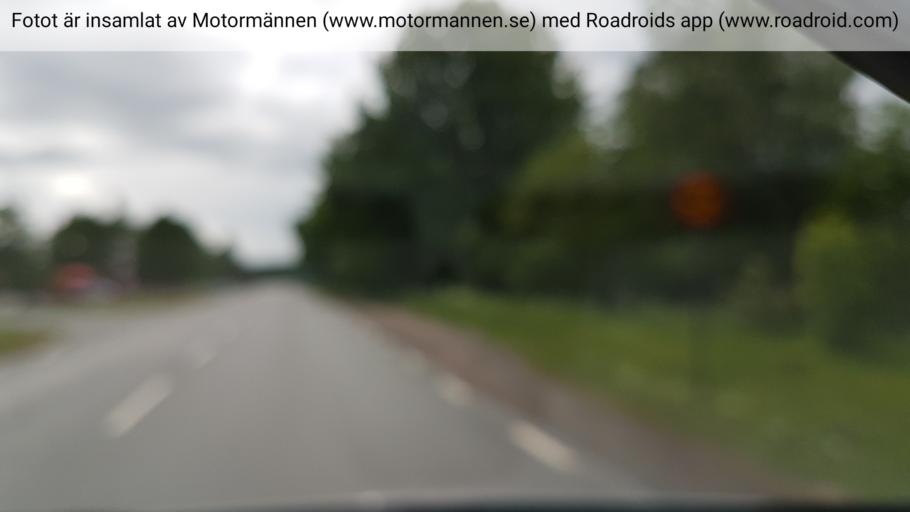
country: SE
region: Joenkoeping
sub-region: Jonkopings Kommun
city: Graenna
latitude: 57.9958
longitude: 14.4407
